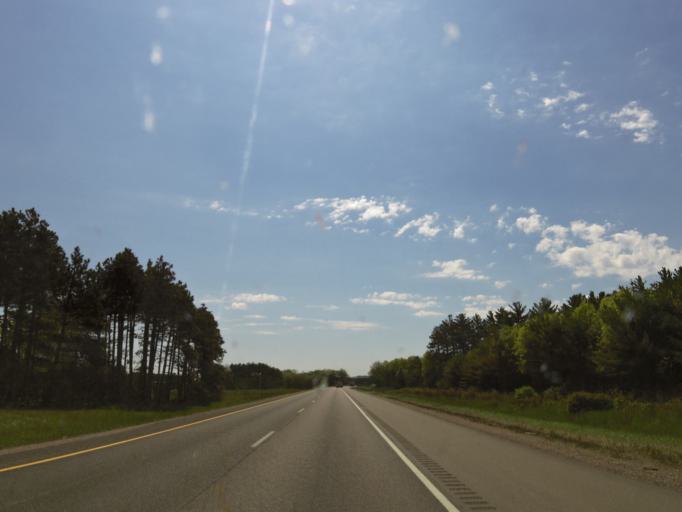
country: US
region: Wisconsin
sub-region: Trempealeau County
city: Osseo
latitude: 44.5496
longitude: -91.1668
